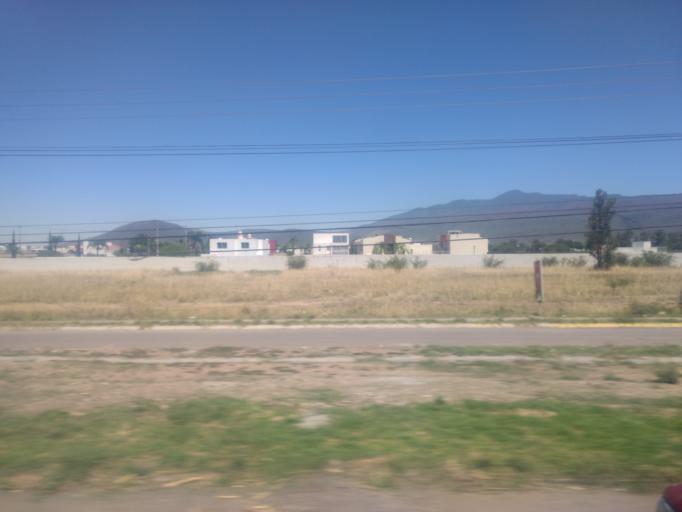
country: MX
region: Jalisco
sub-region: Tlajomulco de Zuniga
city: Santa Cruz de las Flores
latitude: 20.4595
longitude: -103.5135
